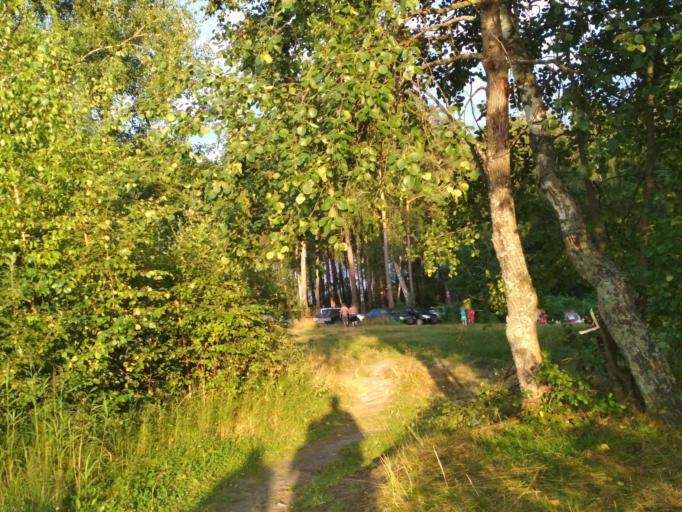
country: RU
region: Rjazan
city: Solotcha
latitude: 54.8273
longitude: 39.9556
